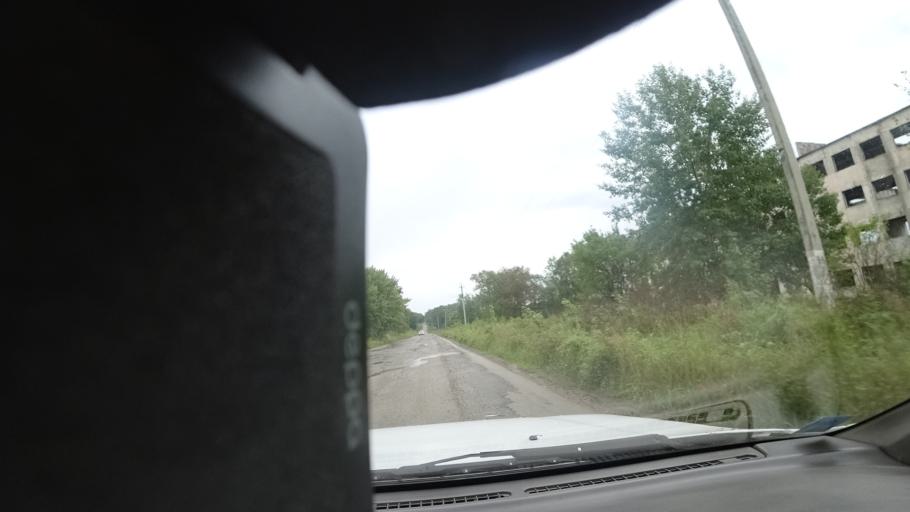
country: RU
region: Primorskiy
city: Lazo
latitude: 45.8699
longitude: 133.6770
